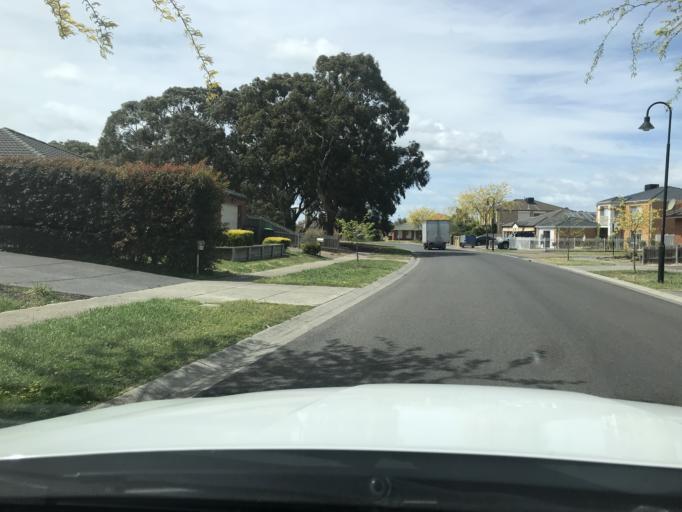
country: AU
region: Victoria
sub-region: Hume
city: Roxburgh Park
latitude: -37.6141
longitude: 144.9280
